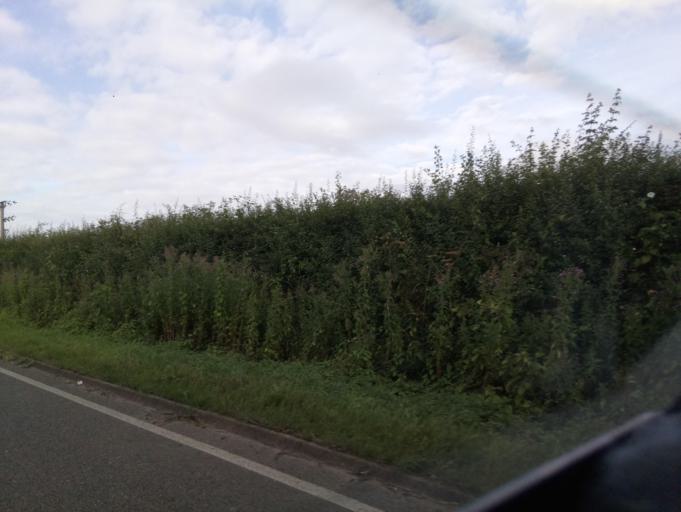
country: GB
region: England
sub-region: Warwickshire
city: Dunchurch
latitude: 52.3262
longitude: -1.3014
